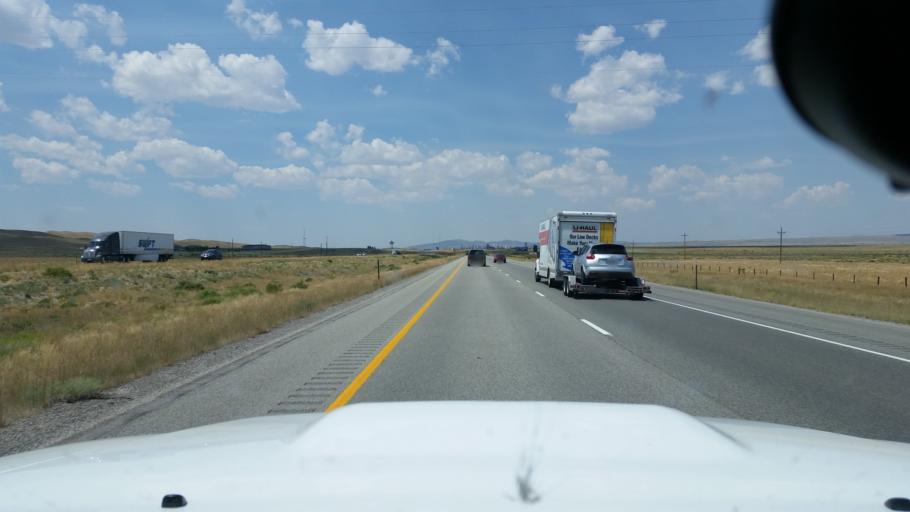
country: US
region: Wyoming
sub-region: Carbon County
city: Rawlins
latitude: 41.7710
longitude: -107.0559
